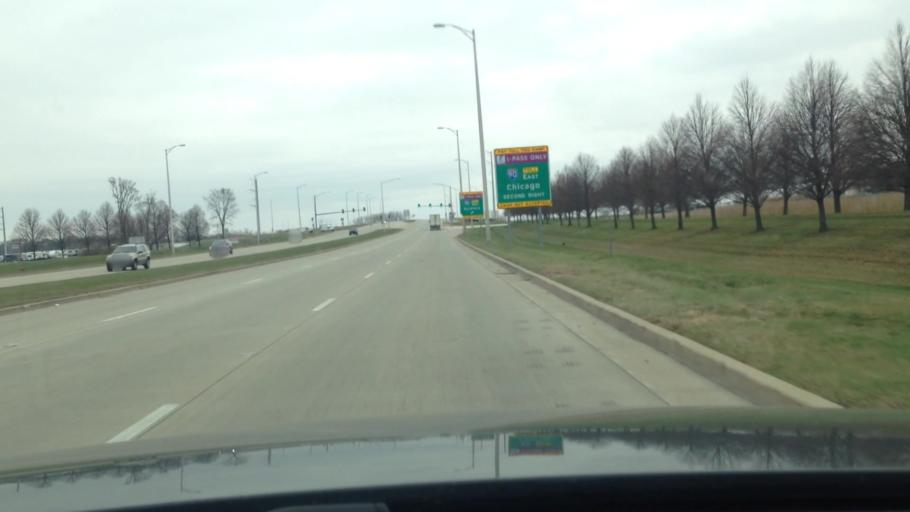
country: US
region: Illinois
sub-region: McHenry County
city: Huntley
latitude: 42.1278
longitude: -88.4335
